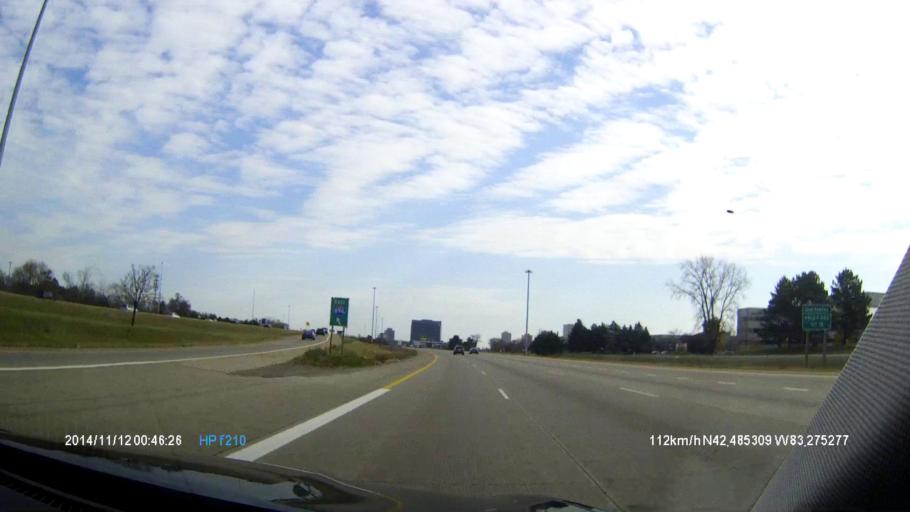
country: US
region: Michigan
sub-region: Oakland County
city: Bingham Farms
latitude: 42.4854
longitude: -83.2757
